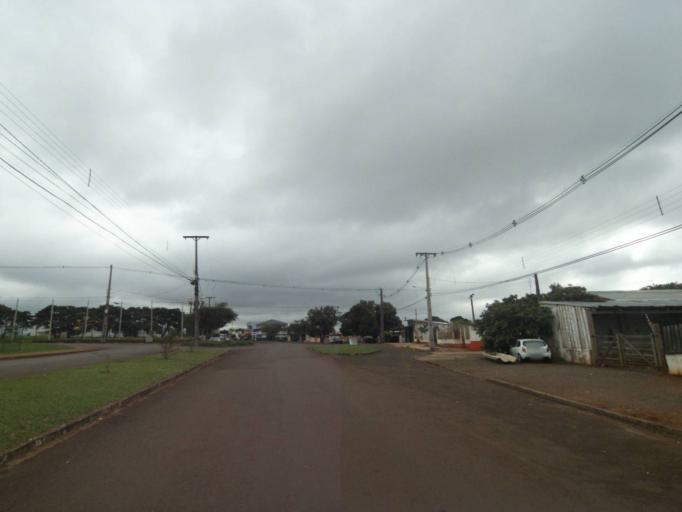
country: BR
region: Parana
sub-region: Campo Mourao
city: Campo Mourao
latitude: -24.0212
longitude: -52.3557
